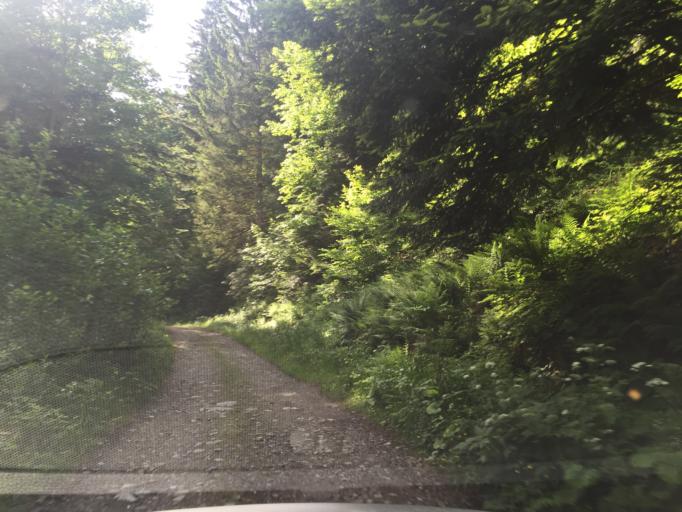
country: FR
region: Rhone-Alpes
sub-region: Departement de la Savoie
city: La Rochette
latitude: 45.4370
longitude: 6.1562
